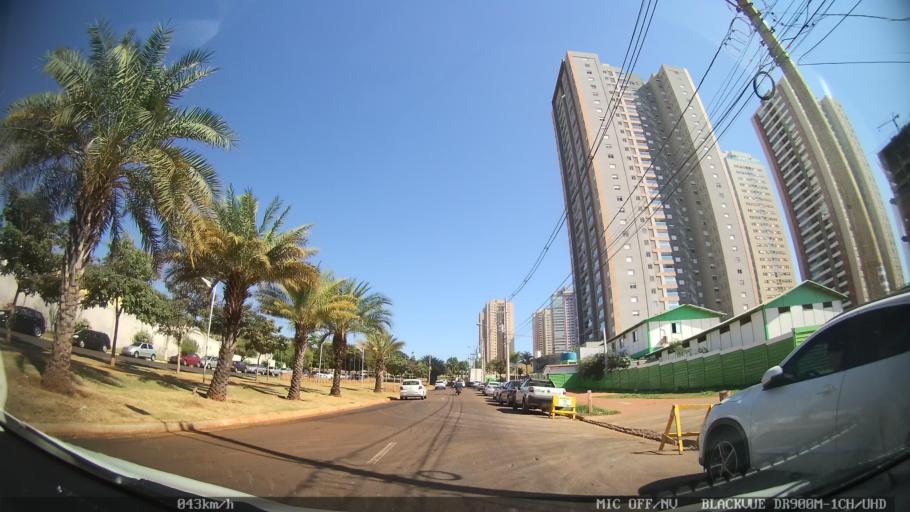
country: BR
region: Sao Paulo
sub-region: Ribeirao Preto
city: Ribeirao Preto
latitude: -21.2192
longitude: -47.7992
